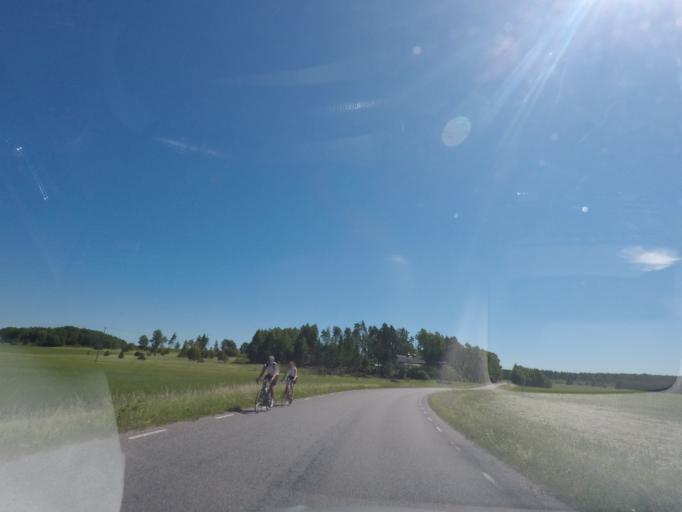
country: SE
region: Uppsala
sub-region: Enkopings Kommun
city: Irsta
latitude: 59.6766
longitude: 16.8652
